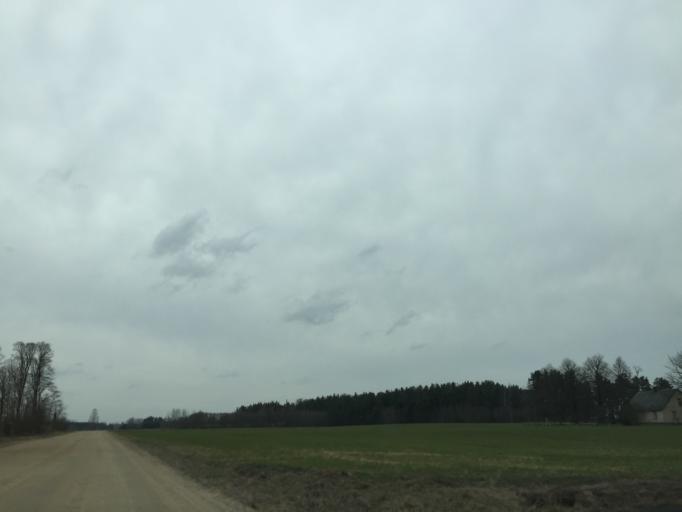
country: LV
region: Livani
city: Livani
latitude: 56.3101
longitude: 26.1641
